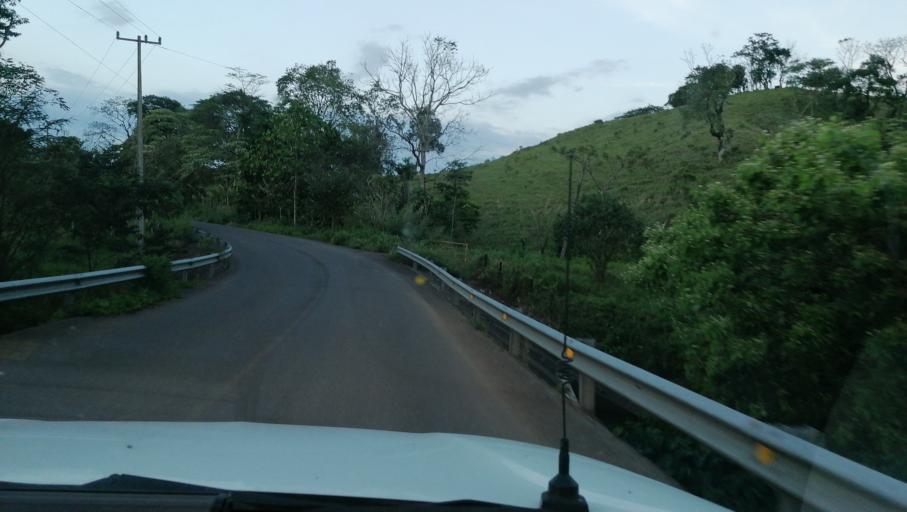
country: MX
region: Chiapas
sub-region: Ostuacan
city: Nuevo Juan del Grijalva
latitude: 17.4335
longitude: -93.3507
